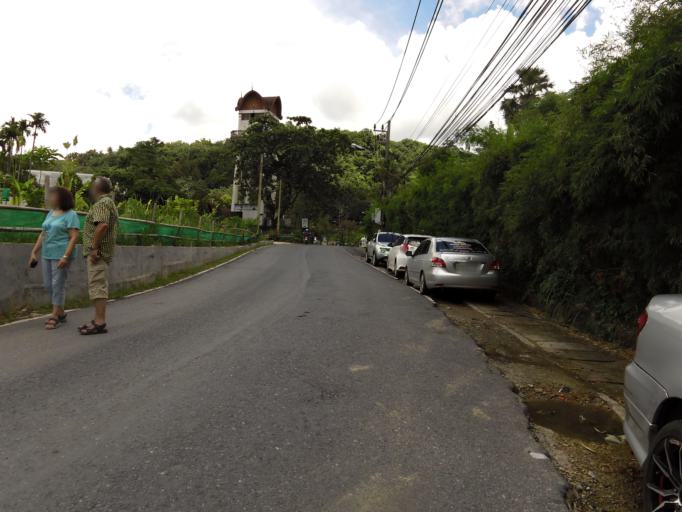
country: TH
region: Phuket
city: Ban Karon
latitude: 7.8548
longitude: 98.2950
